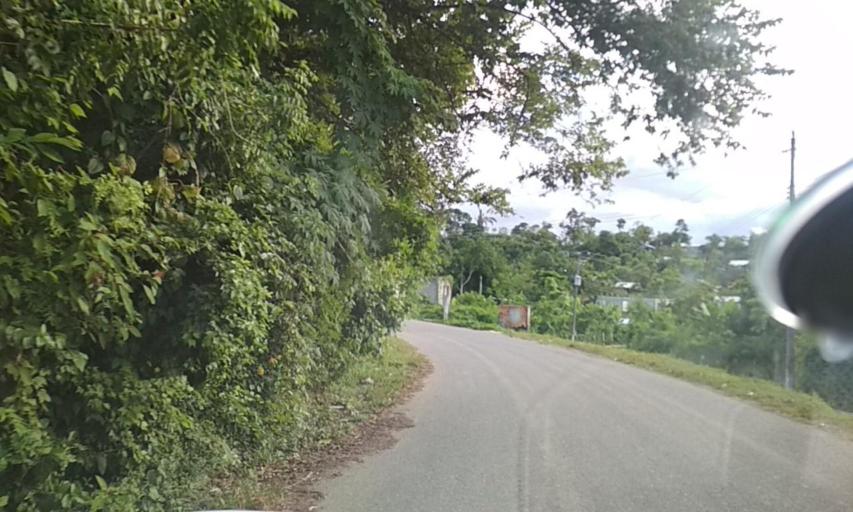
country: MX
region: Veracruz
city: Cazones de Herrera
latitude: 20.6416
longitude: -97.3390
